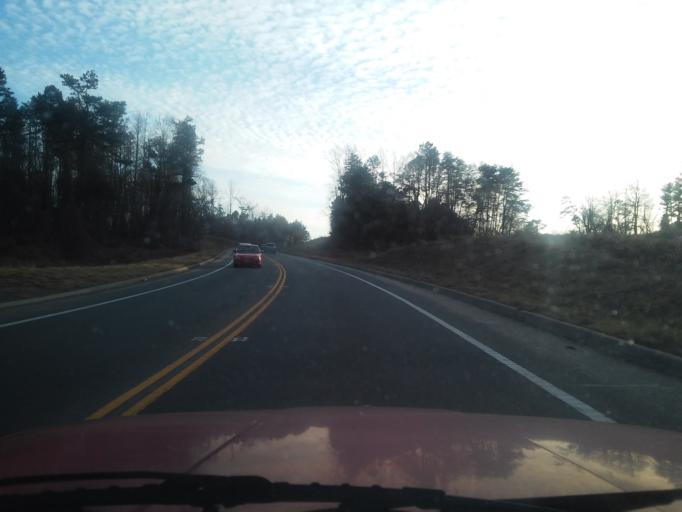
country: US
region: Virginia
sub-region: City of Charlottesville
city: Charlottesville
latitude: 38.0573
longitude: -78.4677
